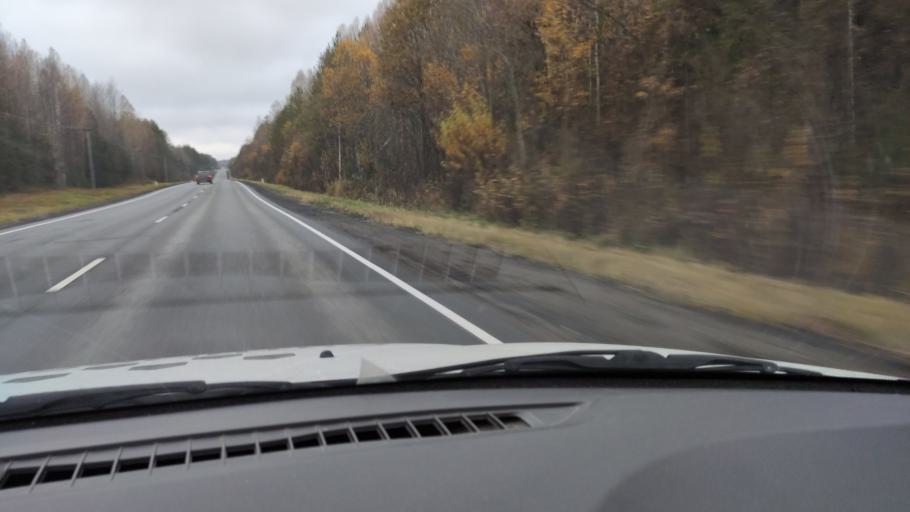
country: RU
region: Kirov
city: Belaya Kholunitsa
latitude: 58.9137
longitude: 51.0785
